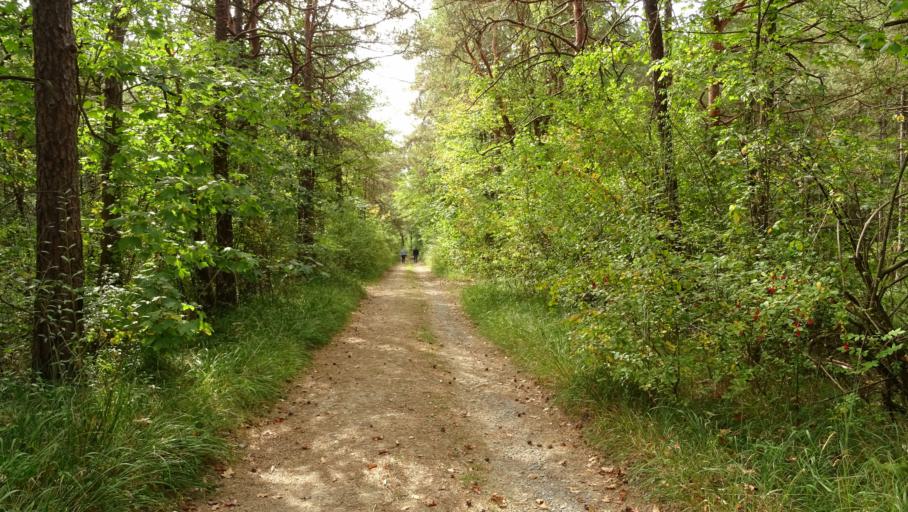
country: DE
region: Baden-Wuerttemberg
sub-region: Karlsruhe Region
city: Mosbach
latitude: 49.3864
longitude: 9.1584
